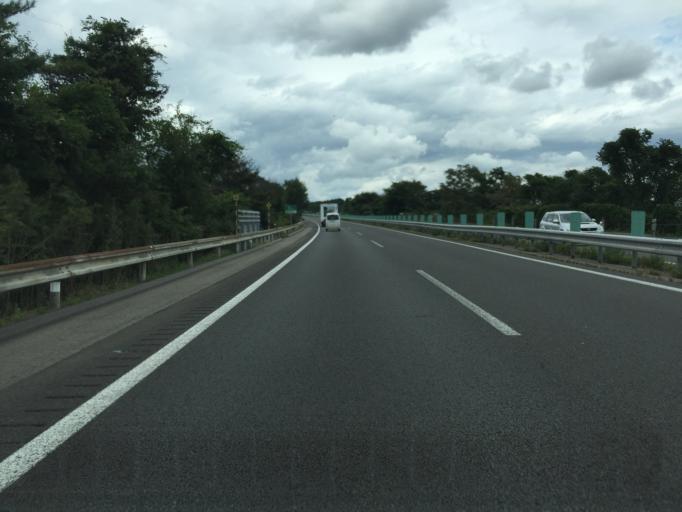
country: JP
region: Miyagi
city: Shiroishi
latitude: 37.9739
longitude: 140.6134
